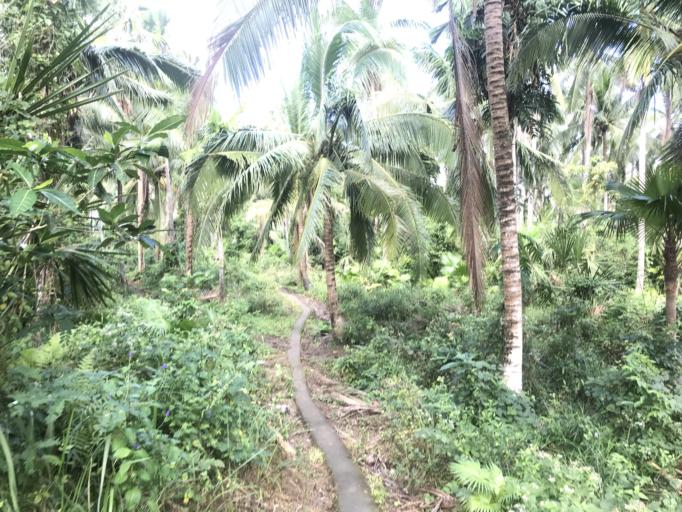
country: PH
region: Calabarzon
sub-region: Province of Quezon
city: Macalelon
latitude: 13.7816
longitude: 122.1419
